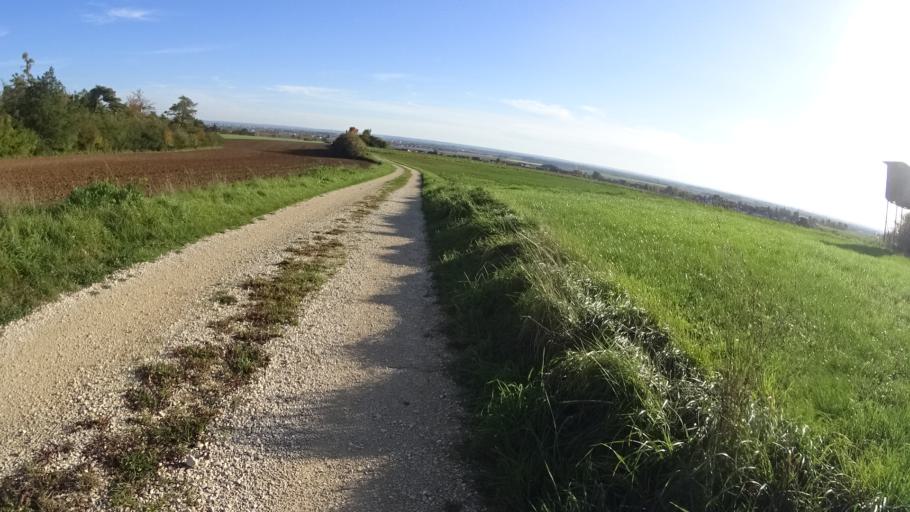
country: DE
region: Bavaria
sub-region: Upper Bavaria
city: Bohmfeld
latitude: 48.8447
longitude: 11.3611
